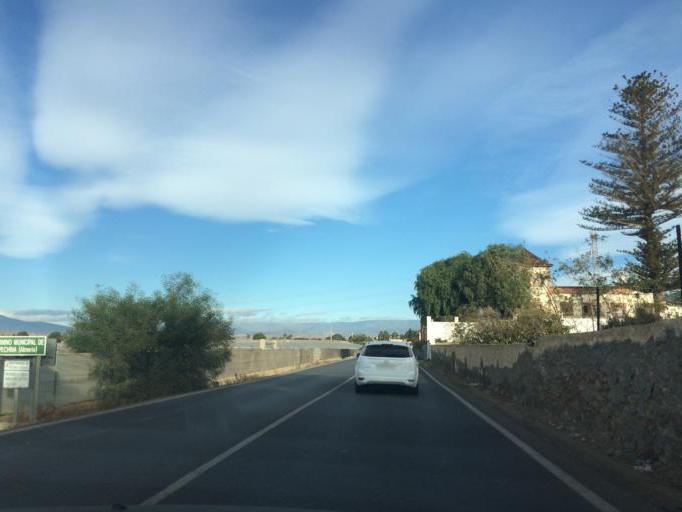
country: ES
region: Andalusia
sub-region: Provincia de Almeria
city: Viator
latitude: 36.8950
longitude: -2.4313
